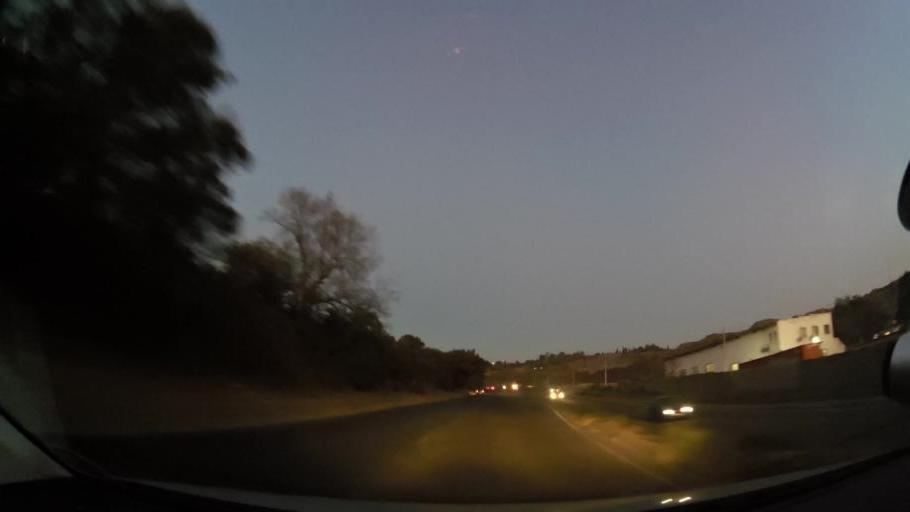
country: ZA
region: Gauteng
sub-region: City of Tshwane Metropolitan Municipality
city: Pretoria
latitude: -25.7717
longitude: 28.1512
